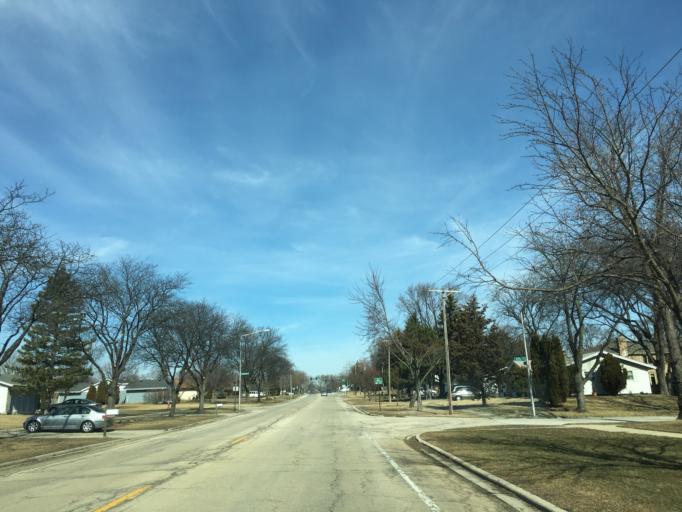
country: US
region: Illinois
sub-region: DuPage County
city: Hanover Park
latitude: 42.0228
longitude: -88.1289
